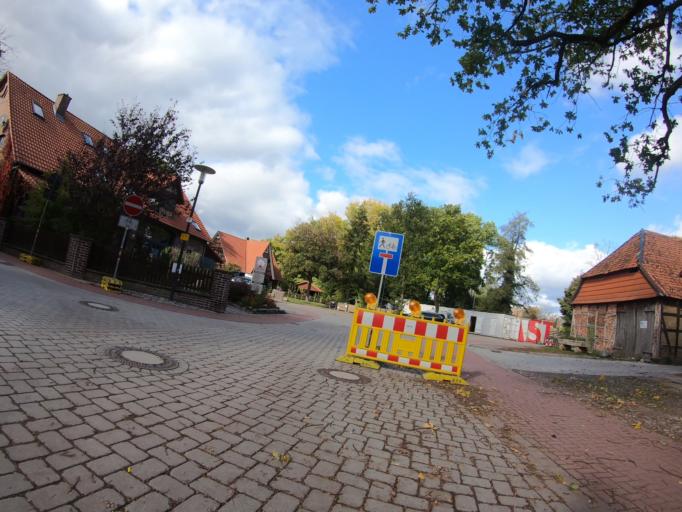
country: DE
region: Lower Saxony
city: Isenbuttel
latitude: 52.4365
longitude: 10.5763
